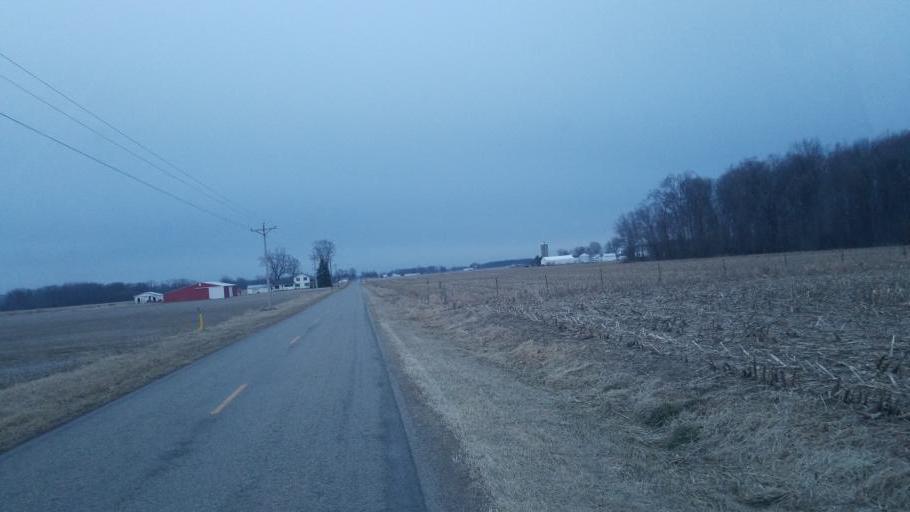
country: US
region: Ohio
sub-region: Defiance County
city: Hicksville
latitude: 41.3326
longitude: -84.7286
